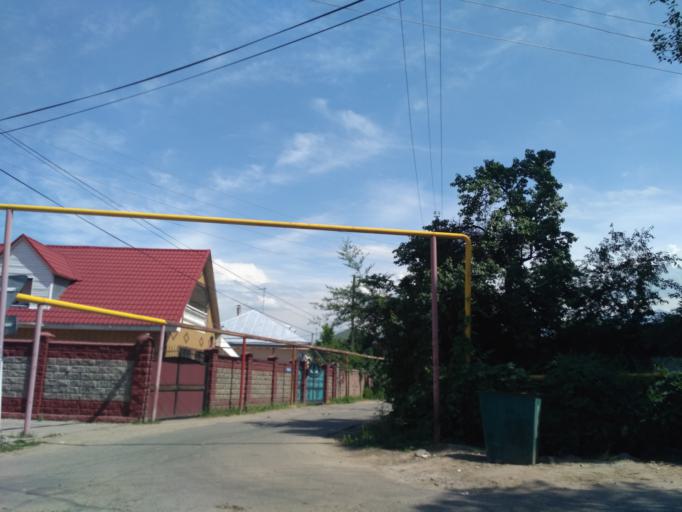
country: KZ
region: Almaty Oblysy
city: Burunday
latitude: 43.1910
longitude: 76.6207
